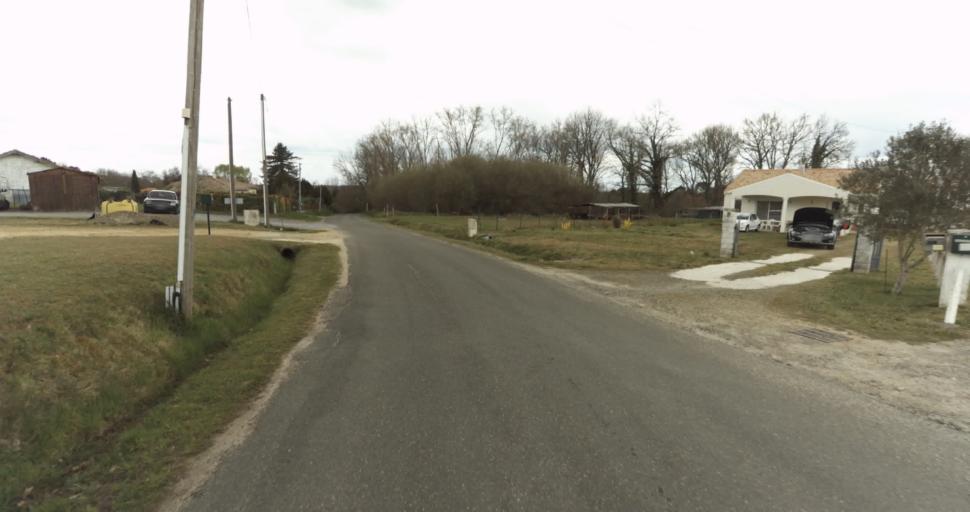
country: FR
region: Aquitaine
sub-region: Departement des Landes
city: Sarbazan
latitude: 44.0265
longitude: -0.3127
